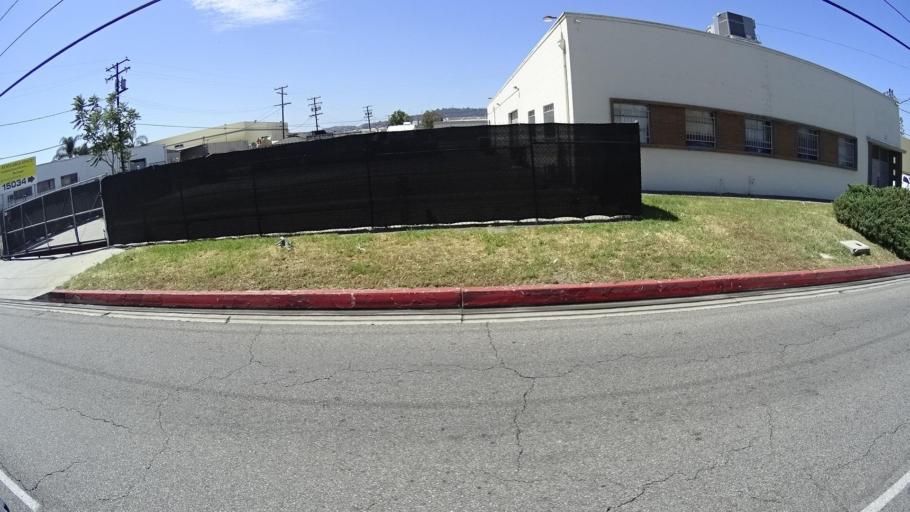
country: US
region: California
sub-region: Los Angeles County
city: La Puente
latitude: 34.0266
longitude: -117.9699
